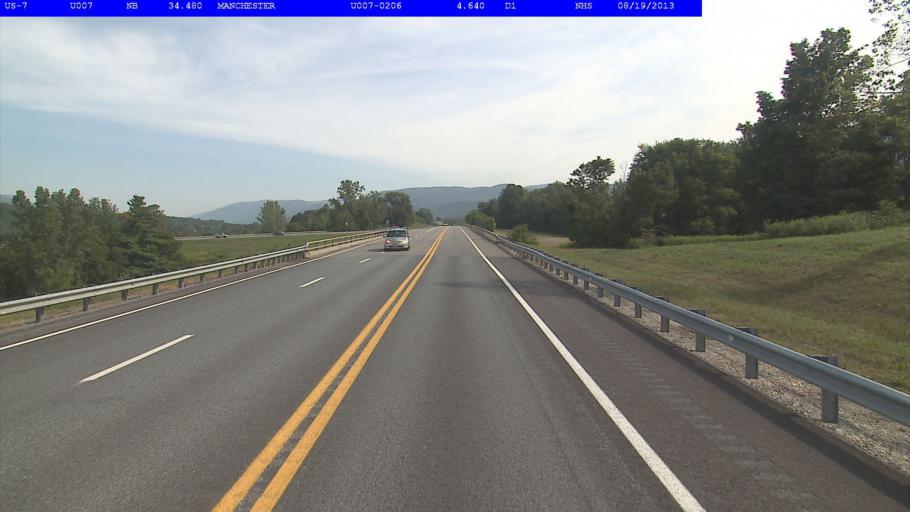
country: US
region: Vermont
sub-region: Bennington County
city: Manchester Center
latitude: 43.1737
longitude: -73.0320
